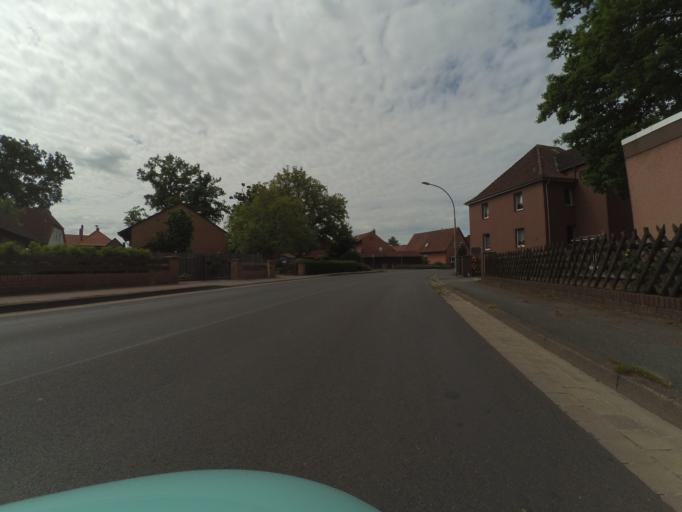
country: DE
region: Lower Saxony
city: Gross Munzel
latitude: 52.4286
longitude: 9.5111
